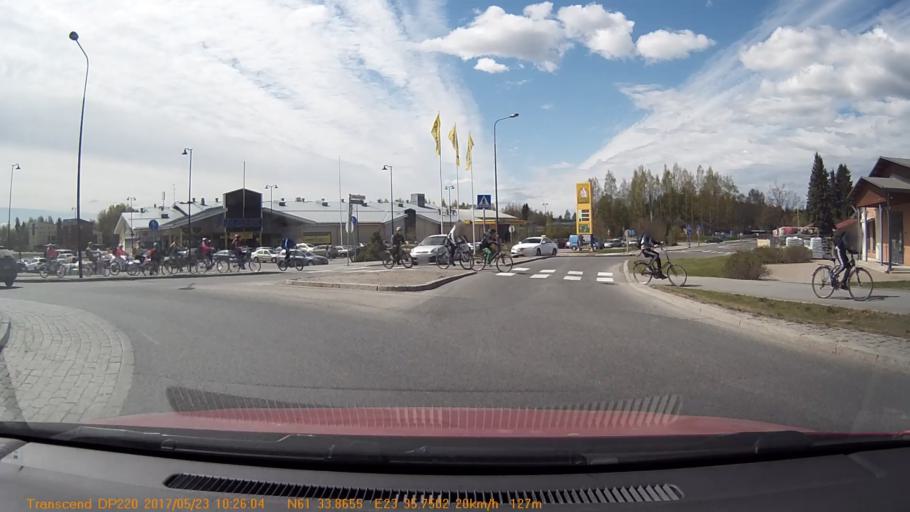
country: FI
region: Pirkanmaa
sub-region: Tampere
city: Yloejaervi
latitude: 61.5644
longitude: 23.5959
